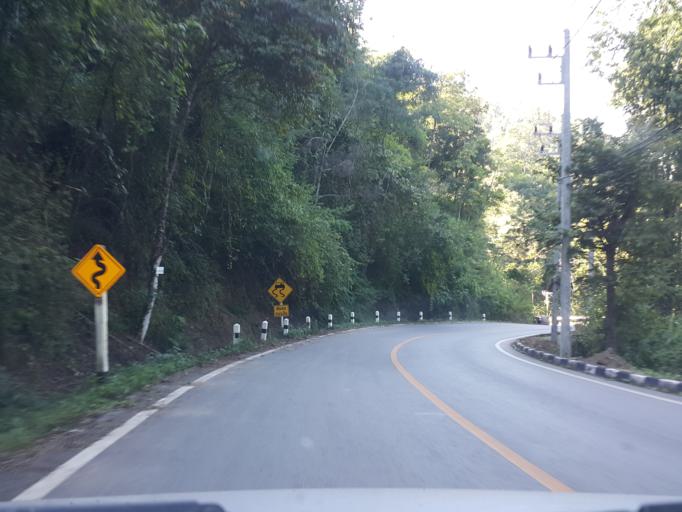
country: TH
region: Mae Hong Son
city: Mae Hi
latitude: 19.2651
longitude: 98.5070
